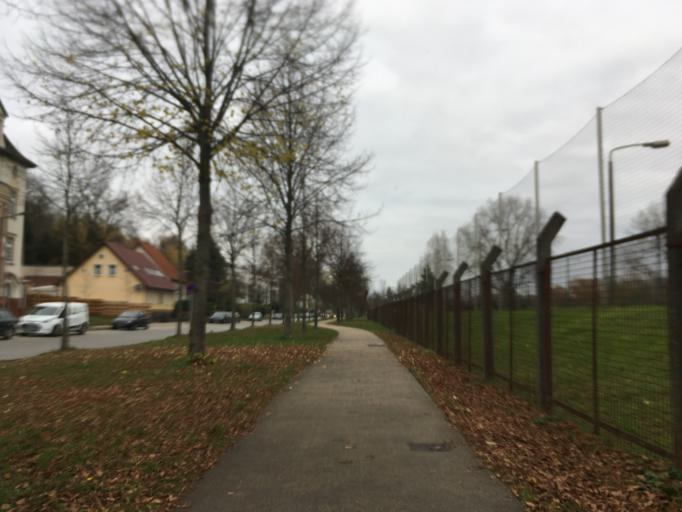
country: DE
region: Brandenburg
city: Frankfurt (Oder)
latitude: 52.3249
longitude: 14.5541
